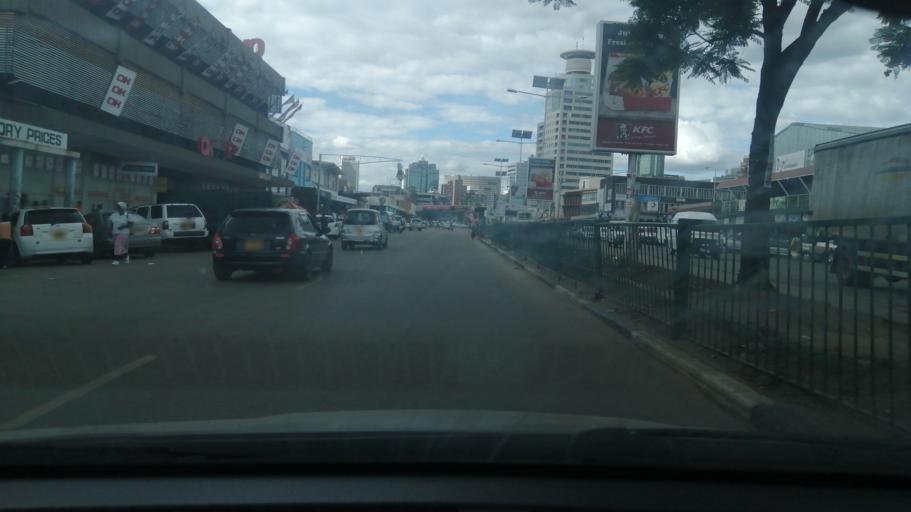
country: ZW
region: Harare
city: Harare
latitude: -17.8352
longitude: 31.0465
